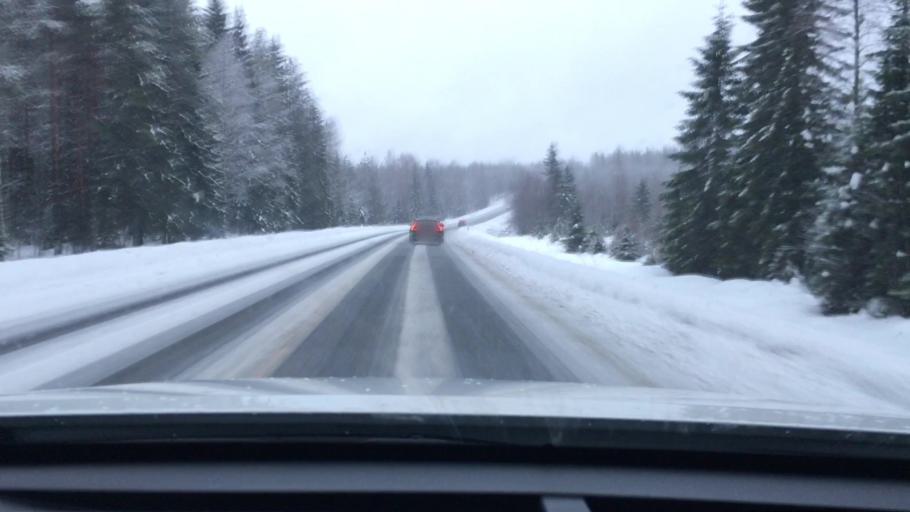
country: FI
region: Northern Savo
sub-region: Ylae-Savo
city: Sonkajaervi
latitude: 63.7708
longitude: 27.4148
